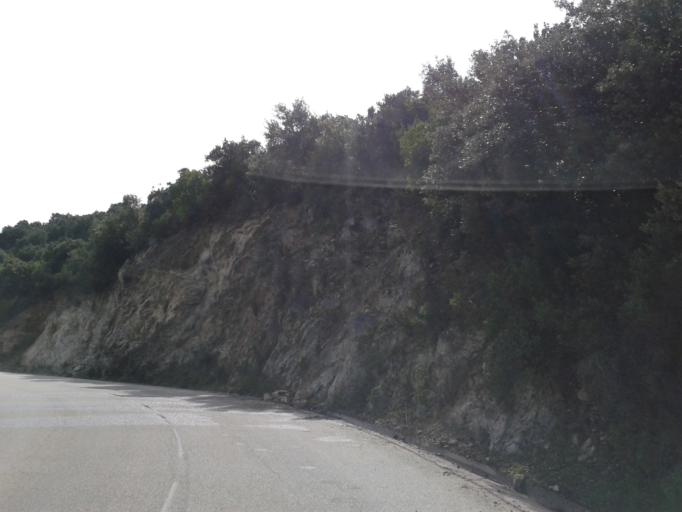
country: FR
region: Corsica
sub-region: Departement de la Haute-Corse
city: Monticello
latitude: 42.6585
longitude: 9.1146
